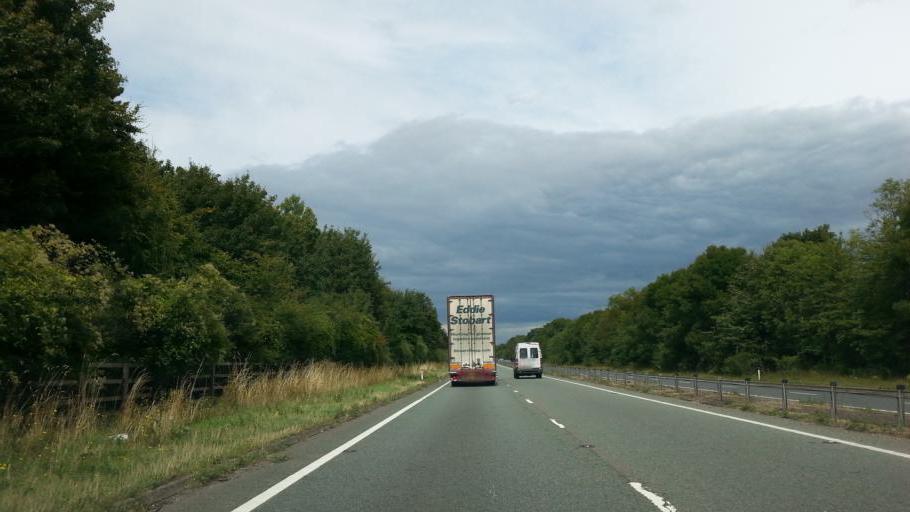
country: GB
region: England
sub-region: Cambridgeshire
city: Sawston
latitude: 52.1108
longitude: 0.2129
